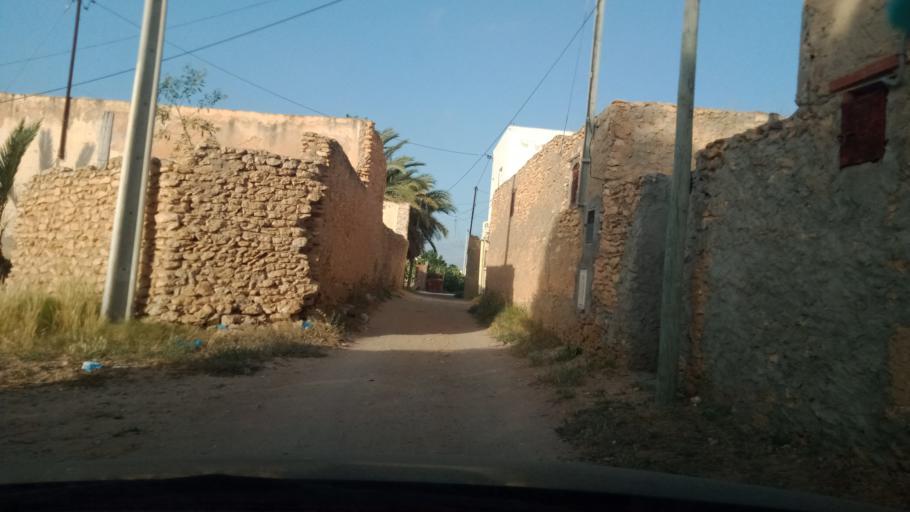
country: TN
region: Safaqis
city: Al Qarmadah
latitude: 34.8208
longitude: 10.7488
